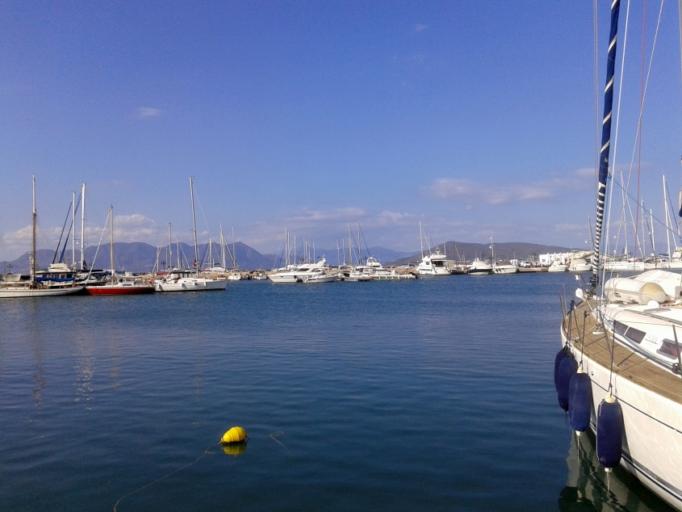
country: GR
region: Attica
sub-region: Nomos Piraios
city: Aegina
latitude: 37.7457
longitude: 23.4290
